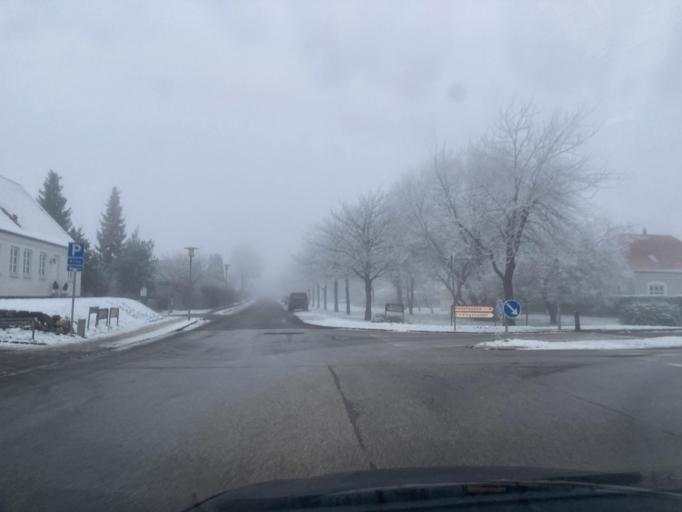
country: DK
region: Zealand
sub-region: Roskilde Kommune
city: Vindinge
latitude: 55.6264
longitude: 12.1385
